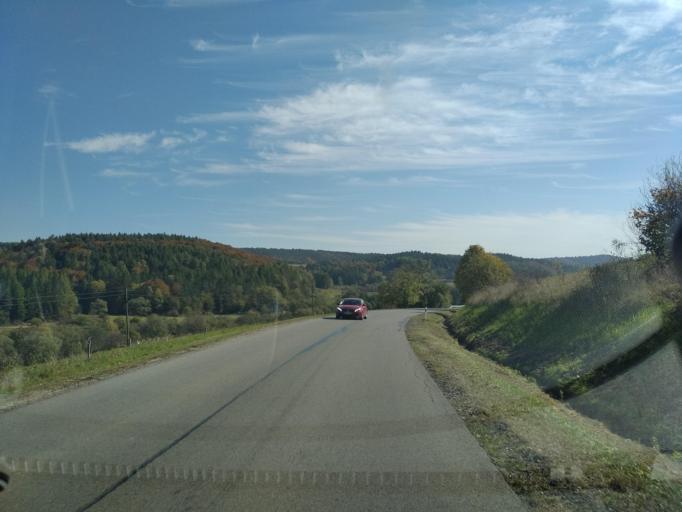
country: PL
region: Subcarpathian Voivodeship
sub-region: Powiat sanocki
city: Komancza
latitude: 49.3628
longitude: 22.0189
